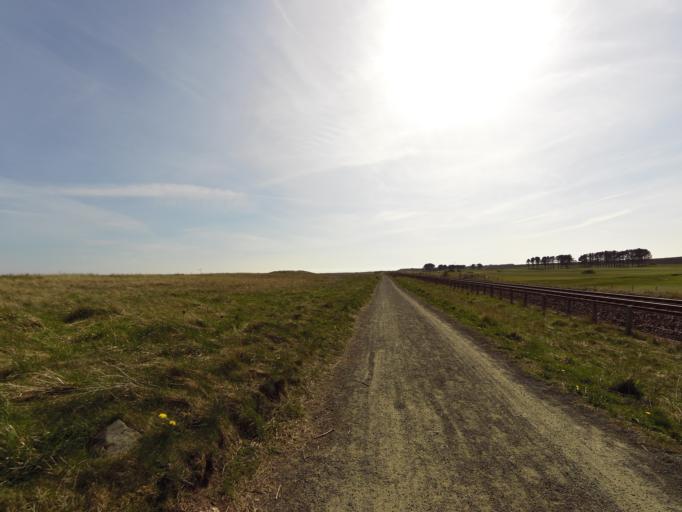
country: GB
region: Scotland
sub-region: Angus
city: Arbroath
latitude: 56.5340
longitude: -2.6314
